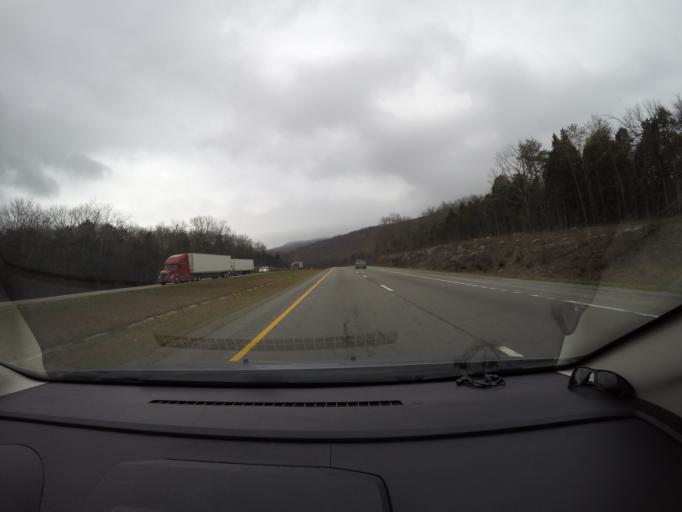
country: US
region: Tennessee
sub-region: Marion County
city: Monteagle
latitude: 35.2735
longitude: -85.8903
